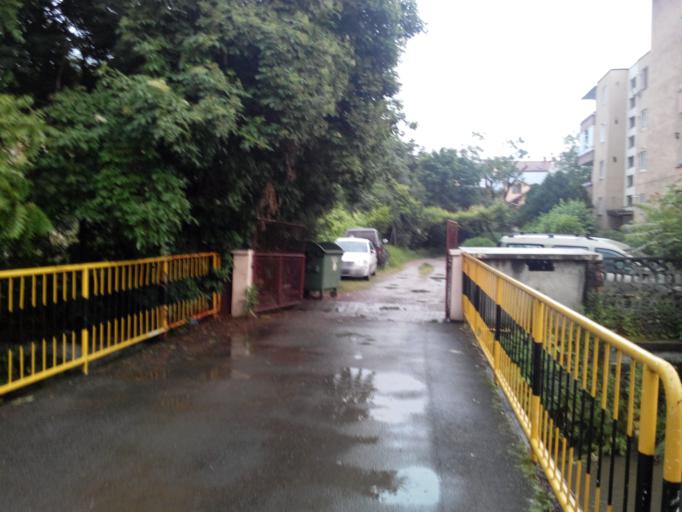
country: RO
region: Cluj
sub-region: Municipiul Cluj-Napoca
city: Cluj-Napoca
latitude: 46.7744
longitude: 23.5963
